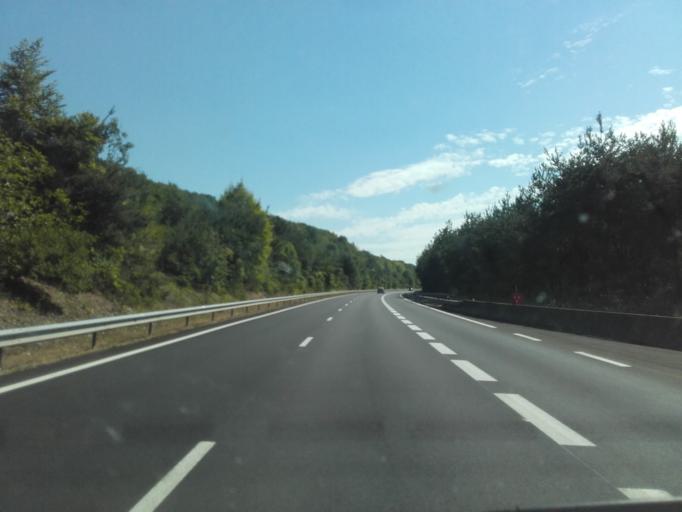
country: FR
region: Bourgogne
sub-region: Departement de la Cote-d'Or
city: Savigny-les-Beaune
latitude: 47.1425
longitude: 4.7015
